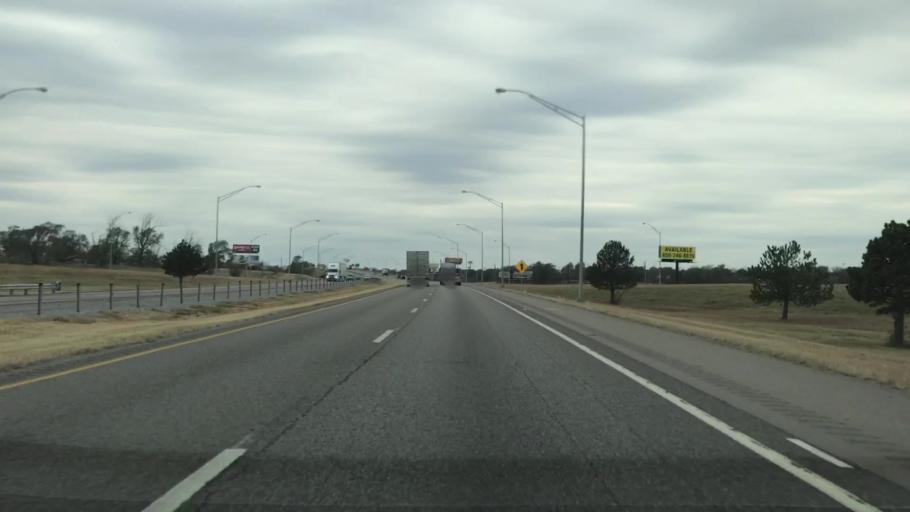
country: US
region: Oklahoma
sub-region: Custer County
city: Clinton
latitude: 35.5007
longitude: -98.9654
